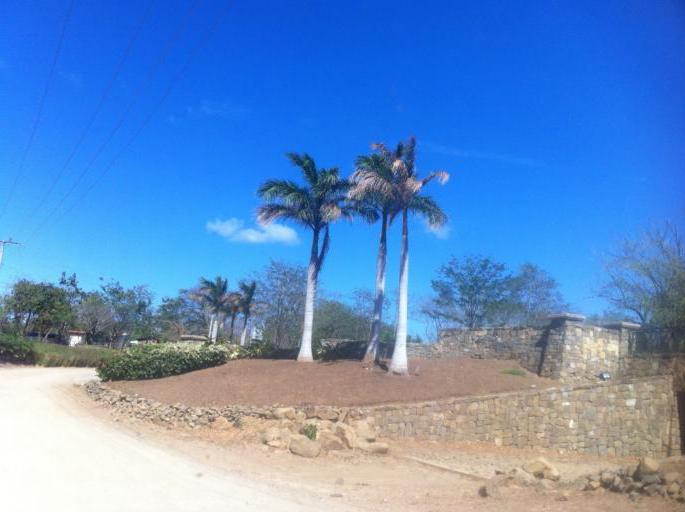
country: NI
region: Rivas
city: Tola
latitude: 11.3889
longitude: -86.0090
